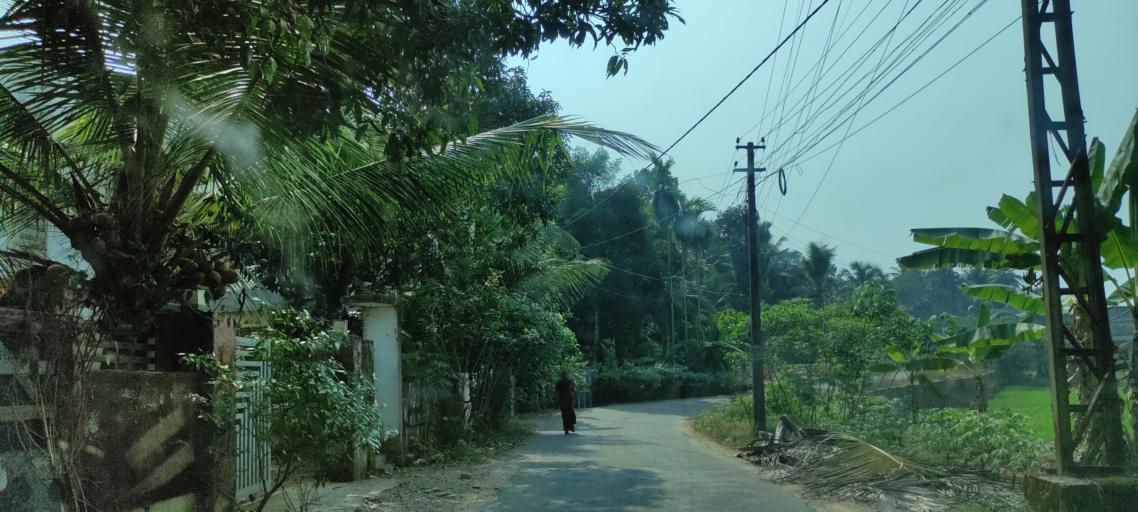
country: IN
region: Kerala
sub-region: Pattanamtitta
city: Tiruvalla
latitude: 9.3603
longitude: 76.5100
